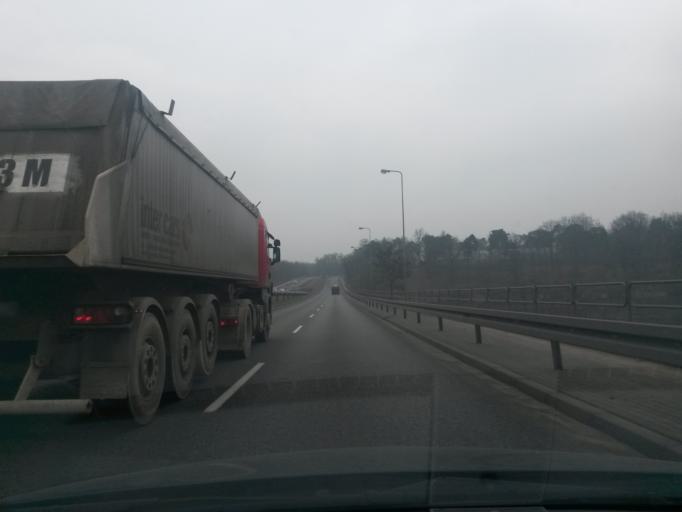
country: PL
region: Masovian Voivodeship
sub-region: Powiat legionowski
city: Nieporet
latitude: 52.4611
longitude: 21.0199
